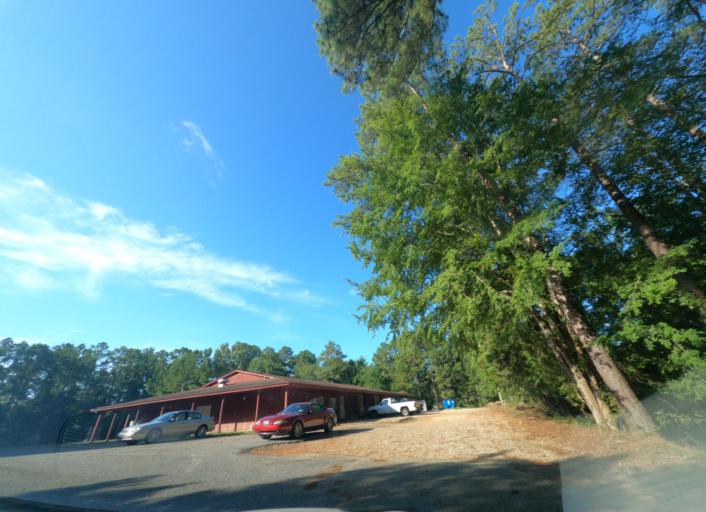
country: US
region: Georgia
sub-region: Lincoln County
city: Lincolnton
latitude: 33.8824
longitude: -82.4147
